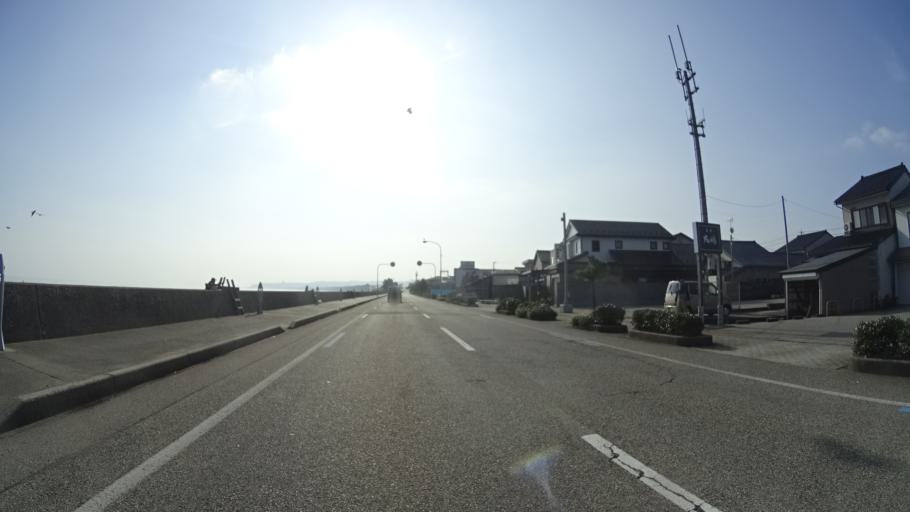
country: JP
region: Toyama
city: Himi
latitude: 36.8509
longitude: 136.9930
